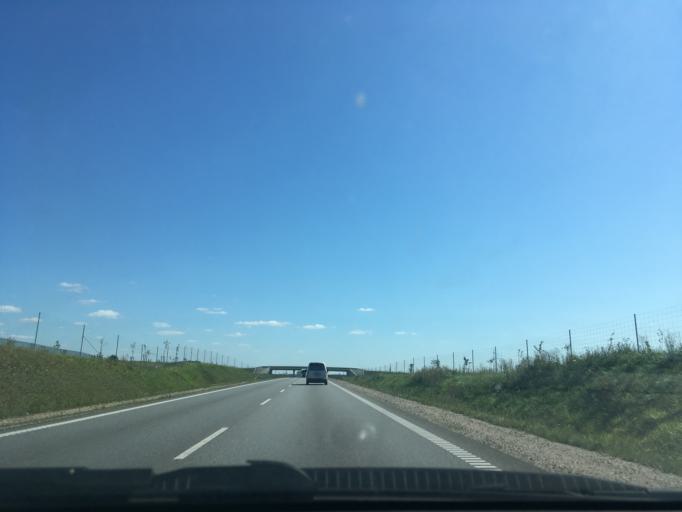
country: PL
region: Podlasie
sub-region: Powiat suwalski
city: Raczki
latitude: 53.9049
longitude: 22.8471
